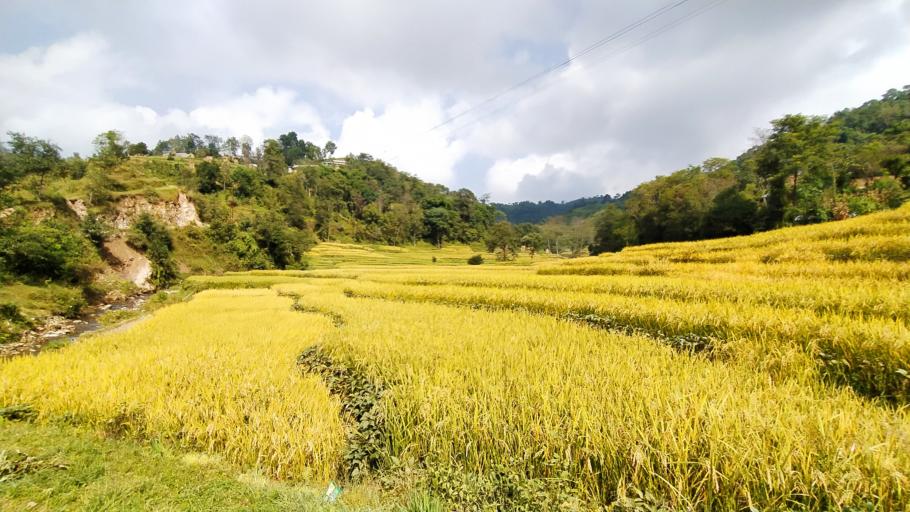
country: NP
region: Central Region
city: Panaoti
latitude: 27.6006
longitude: 85.5007
